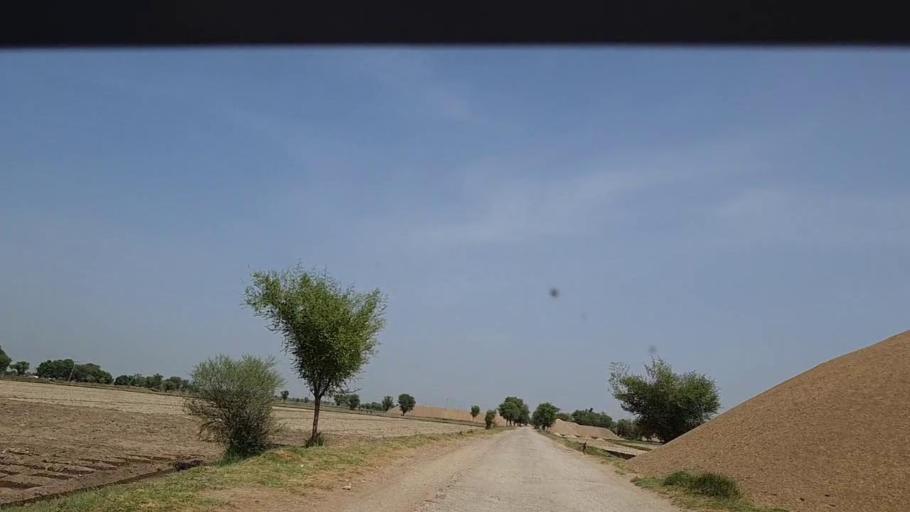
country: PK
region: Sindh
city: Phulji
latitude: 26.9586
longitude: 67.7025
